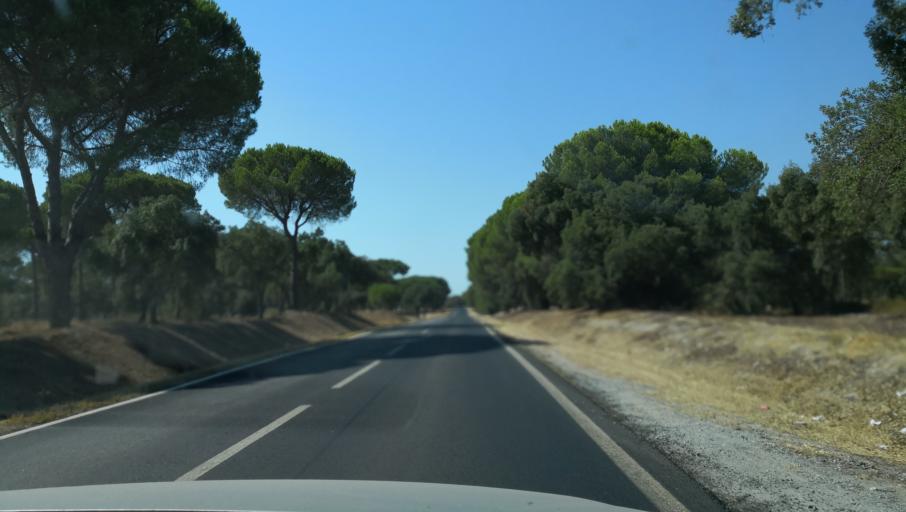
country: PT
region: Setubal
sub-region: Alcacer do Sal
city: Alcacer do Sal
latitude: 38.3625
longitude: -8.5336
